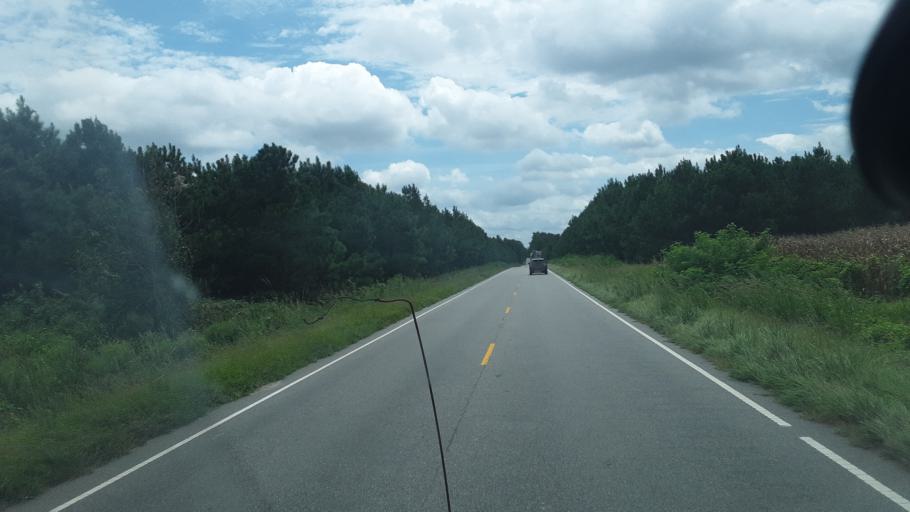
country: US
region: North Carolina
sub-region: Robeson County
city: Rowland
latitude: 34.4884
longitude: -79.2474
